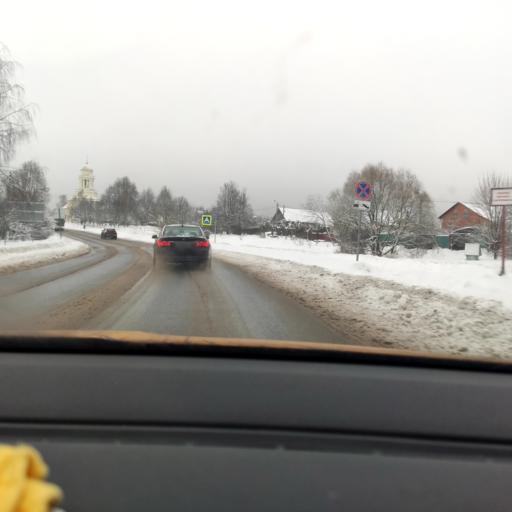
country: RU
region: Moskovskaya
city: Yershovo
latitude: 55.7668
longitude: 36.8600
